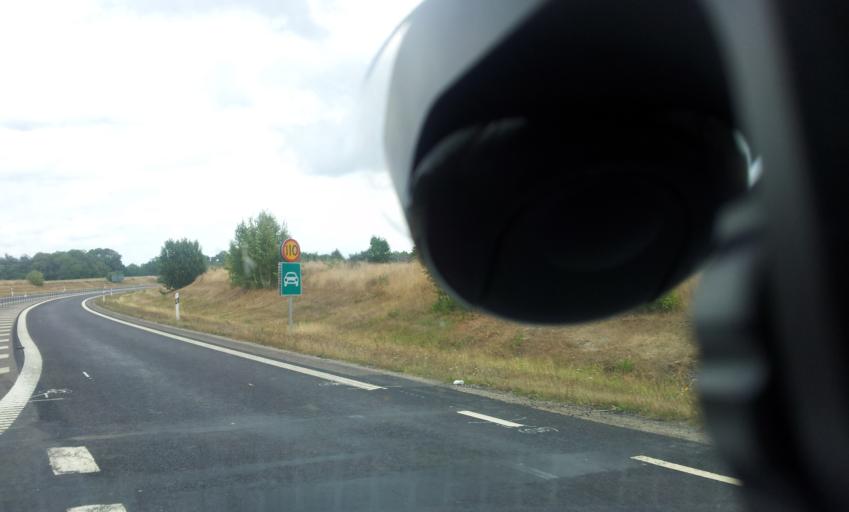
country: SE
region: Kalmar
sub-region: Torsas Kommun
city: Torsas
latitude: 56.4345
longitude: 16.0759
